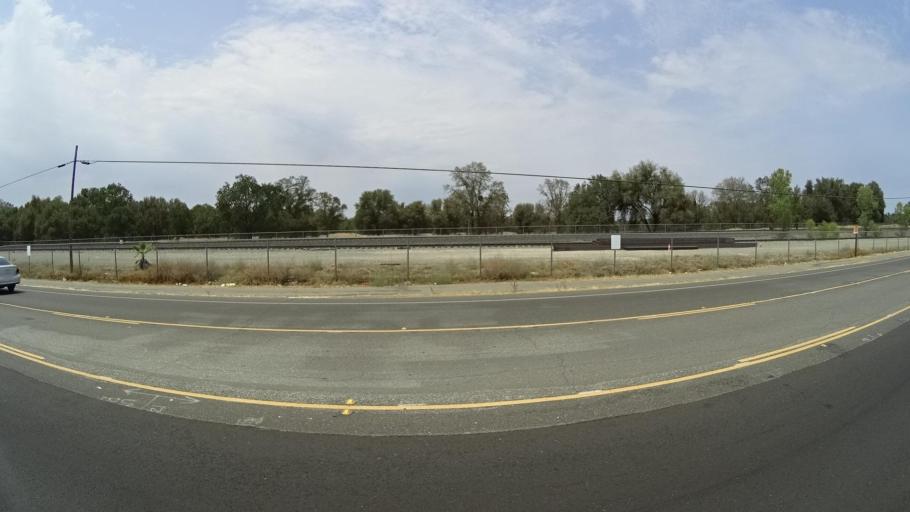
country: US
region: California
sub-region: Placer County
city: Loomis
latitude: 38.8136
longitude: -121.2030
